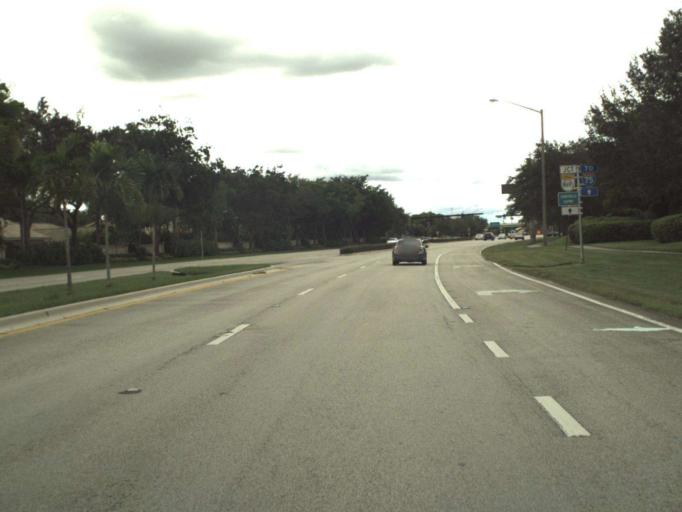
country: US
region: Florida
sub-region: Broward County
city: Coral Springs
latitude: 26.2330
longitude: -80.2903
